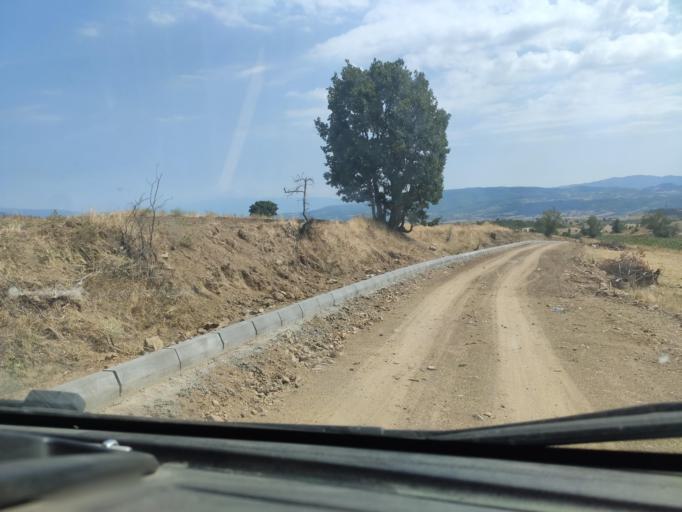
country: MK
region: Radovis
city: Radovish
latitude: 41.6737
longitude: 22.4044
